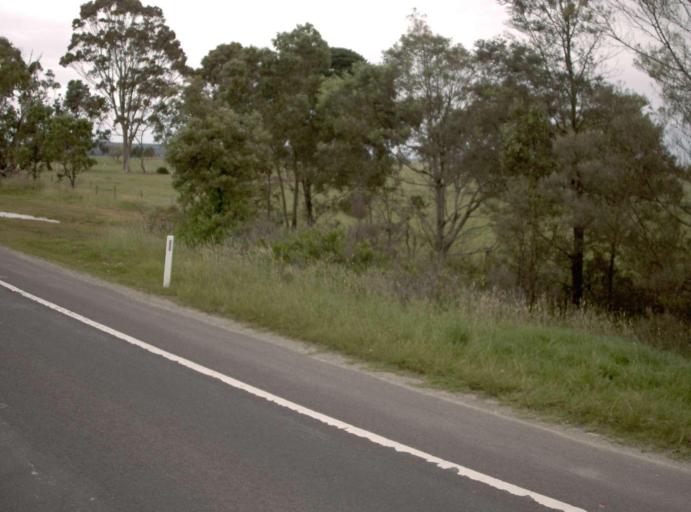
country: AU
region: Victoria
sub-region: Cardinia
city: Koo-Wee-Rup
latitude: -38.2993
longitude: 145.5611
